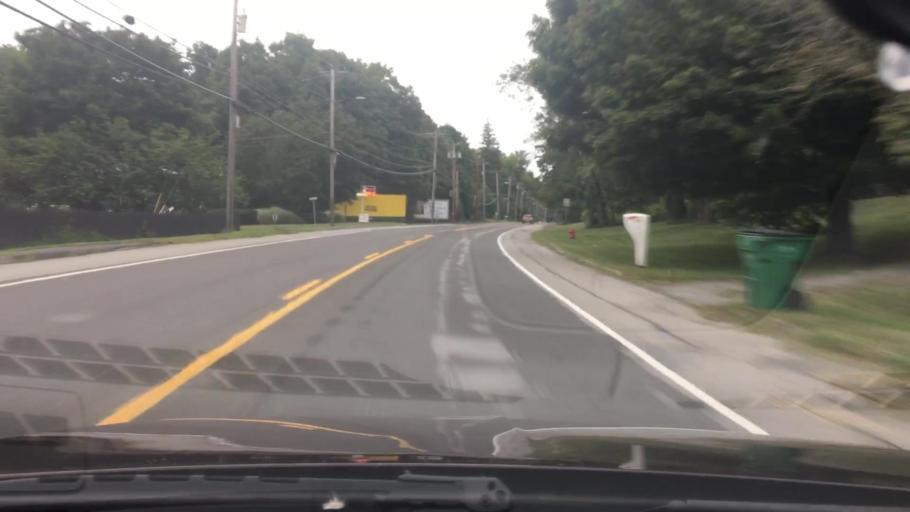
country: US
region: New York
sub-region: Dutchess County
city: Pleasant Valley
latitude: 41.7222
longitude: -73.8464
